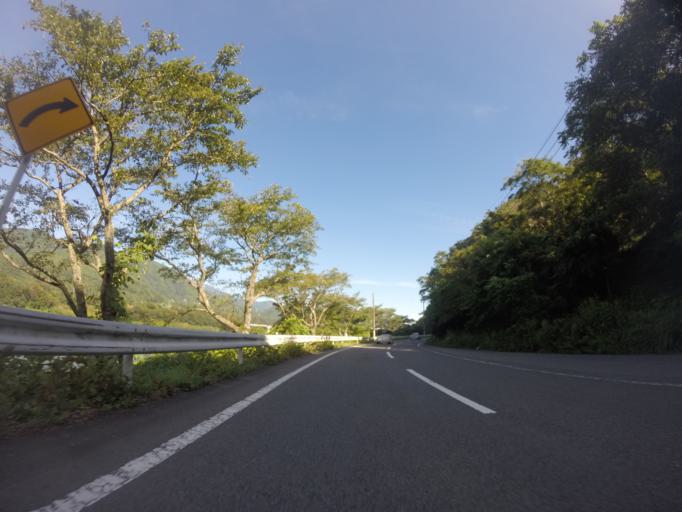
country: JP
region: Shizuoka
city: Fujinomiya
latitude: 35.3026
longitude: 138.4568
